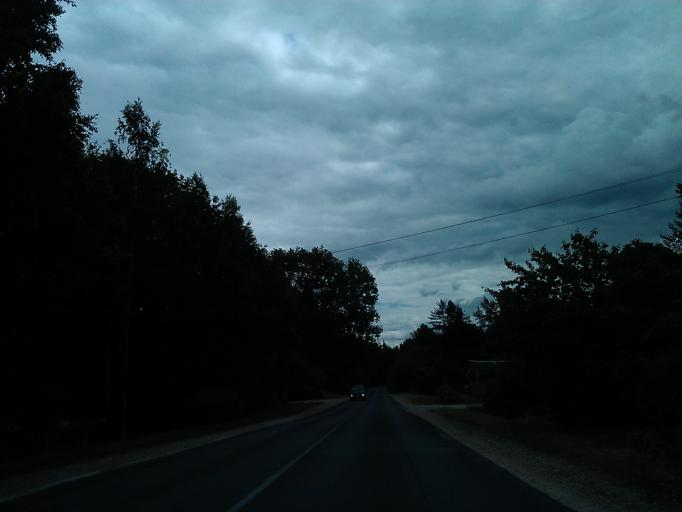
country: LV
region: Dobeles Rajons
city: Dobele
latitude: 56.6428
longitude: 23.2446
